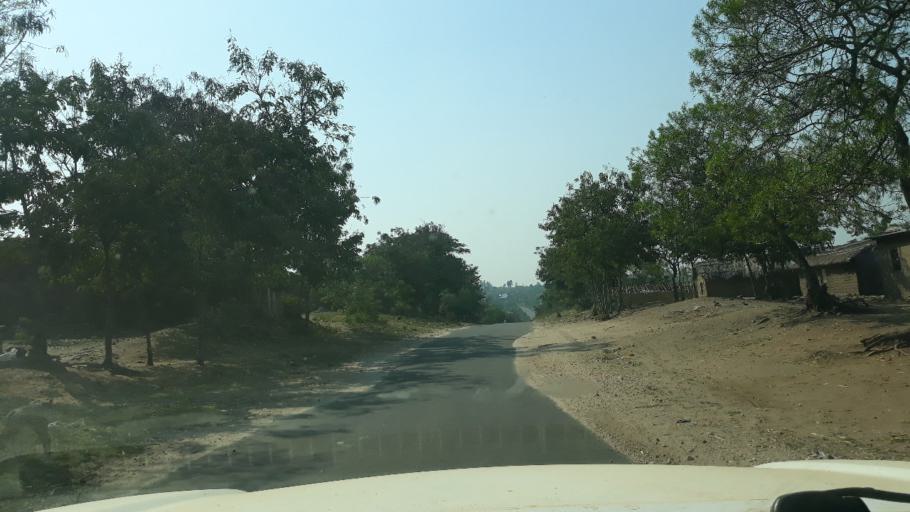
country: CD
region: South Kivu
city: Uvira
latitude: -3.1871
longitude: 29.1530
